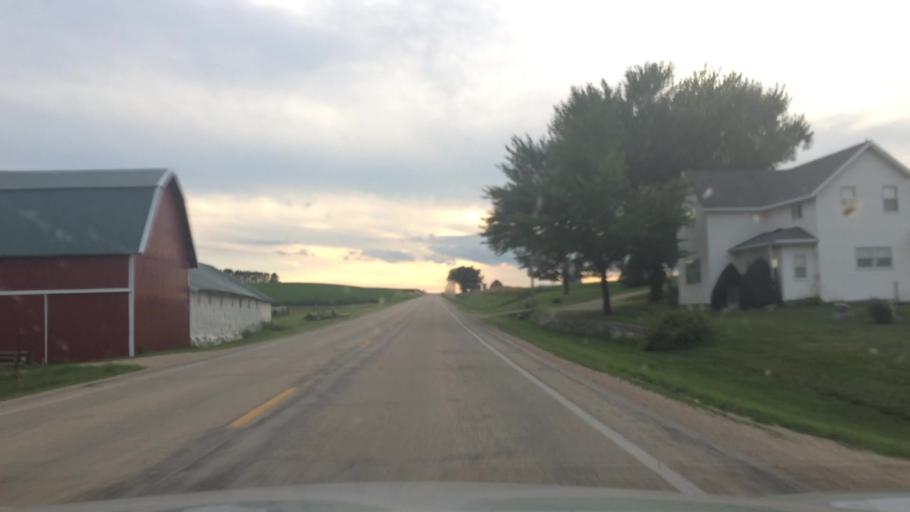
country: US
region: Wisconsin
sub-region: Columbia County
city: Lodi
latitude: 43.2357
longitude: -89.5321
